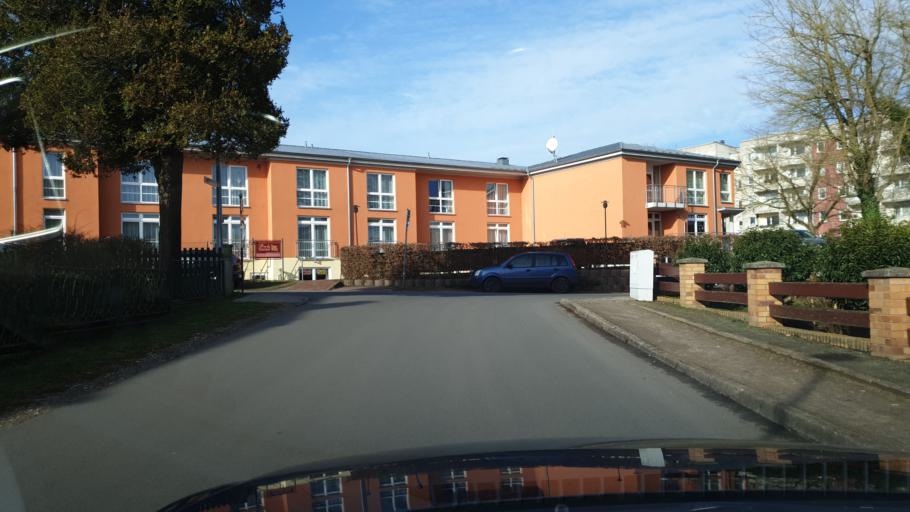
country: DE
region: Mecklenburg-Vorpommern
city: Lankow
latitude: 53.6464
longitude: 11.3564
